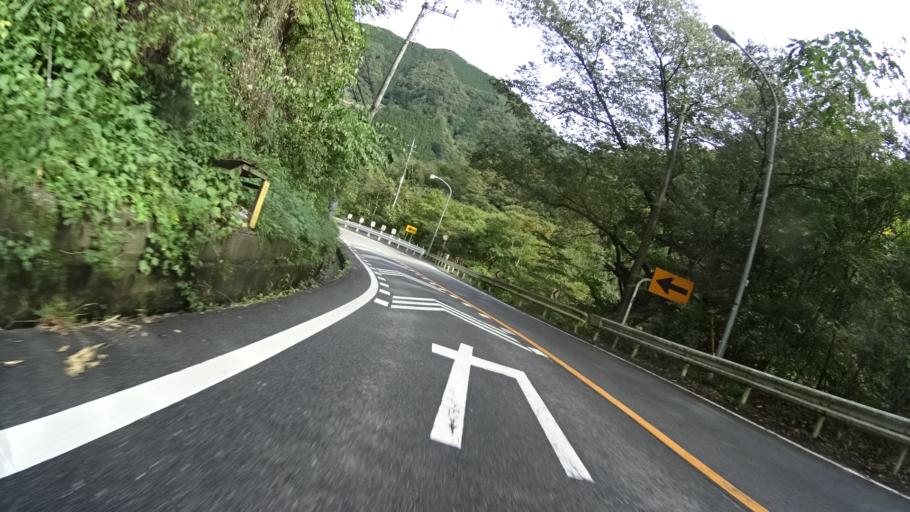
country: JP
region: Yamanashi
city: Otsuki
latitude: 35.7853
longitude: 138.9587
